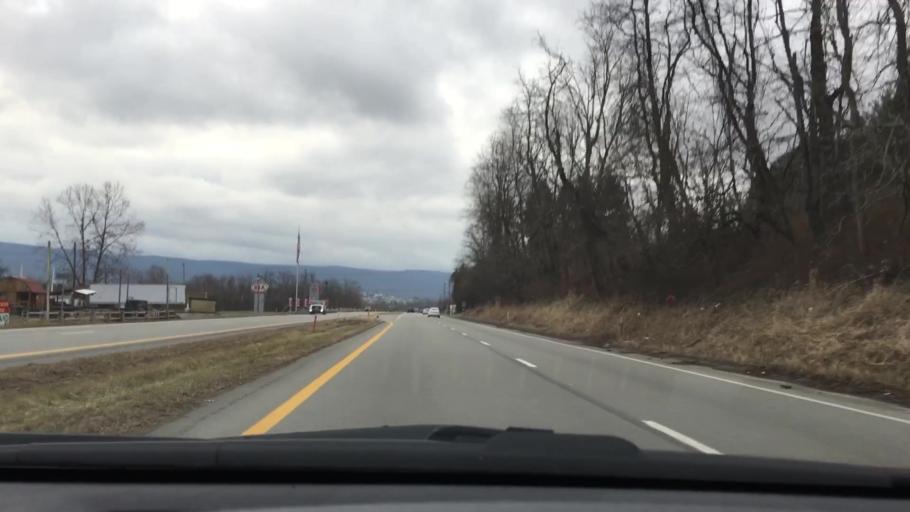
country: US
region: Pennsylvania
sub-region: Fayette County
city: Oliver
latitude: 39.9354
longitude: -79.7302
